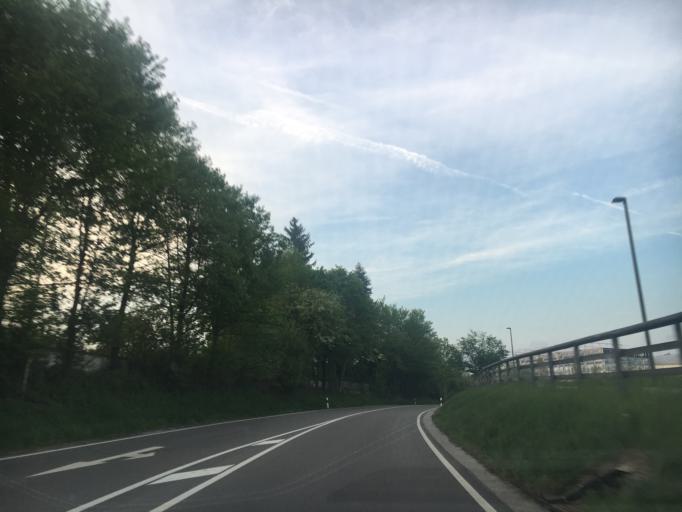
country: DE
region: Bavaria
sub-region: Upper Bavaria
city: Gaissach
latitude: 47.7554
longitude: 11.5753
